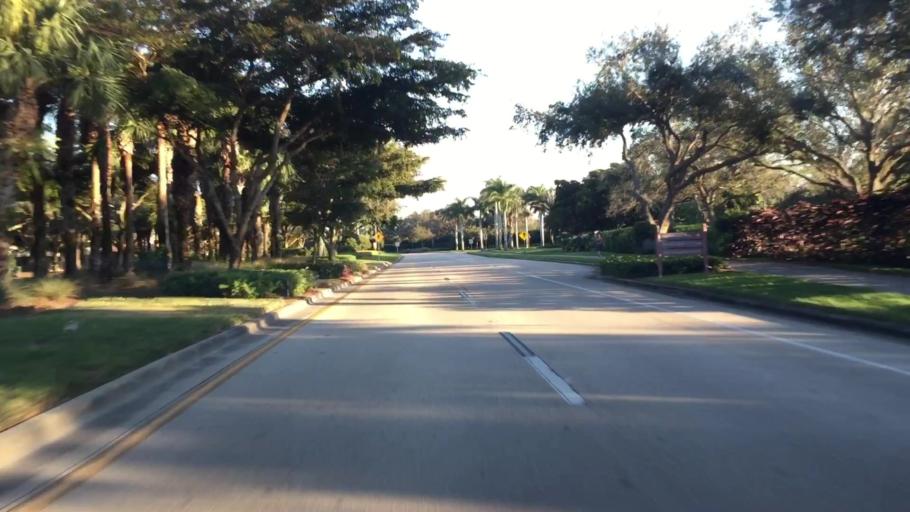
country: US
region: Florida
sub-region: Lee County
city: Estero
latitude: 26.3969
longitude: -81.7964
